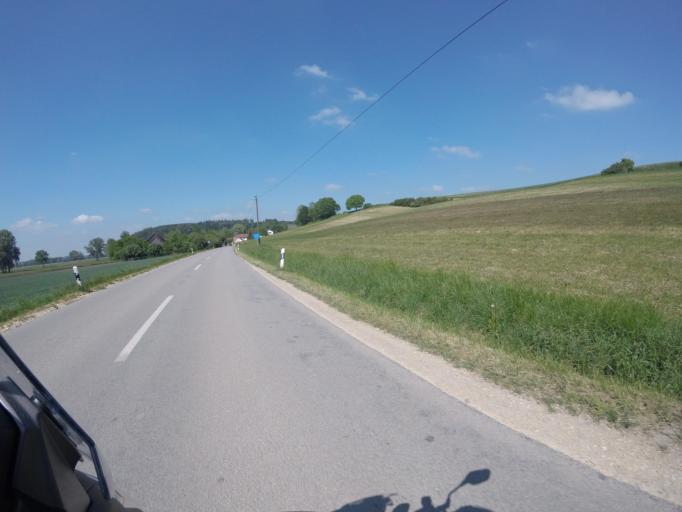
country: DE
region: Bavaria
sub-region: Upper Bavaria
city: Kranzberg
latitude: 48.3802
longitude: 11.6130
